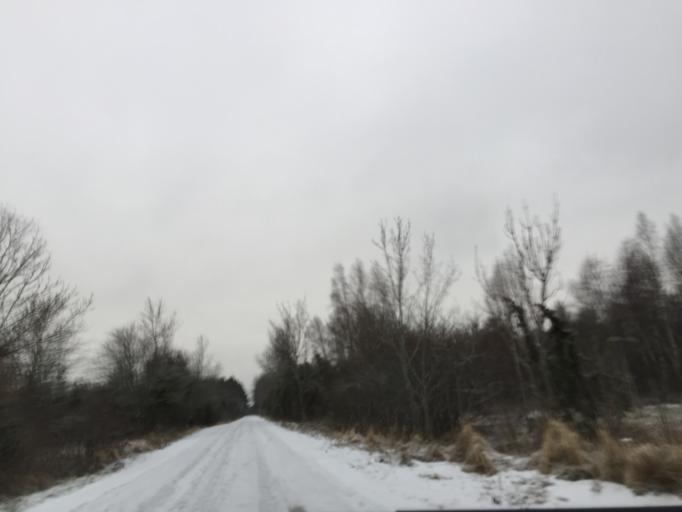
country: EE
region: Saare
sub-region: Orissaare vald
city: Orissaare
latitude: 58.5703
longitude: 23.3834
